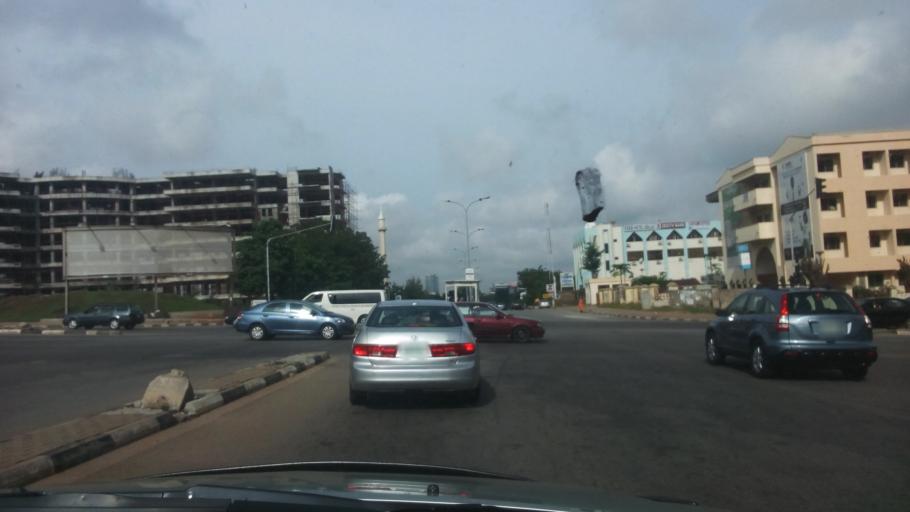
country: NG
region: Abuja Federal Capital Territory
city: Abuja
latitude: 9.0641
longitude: 7.4939
